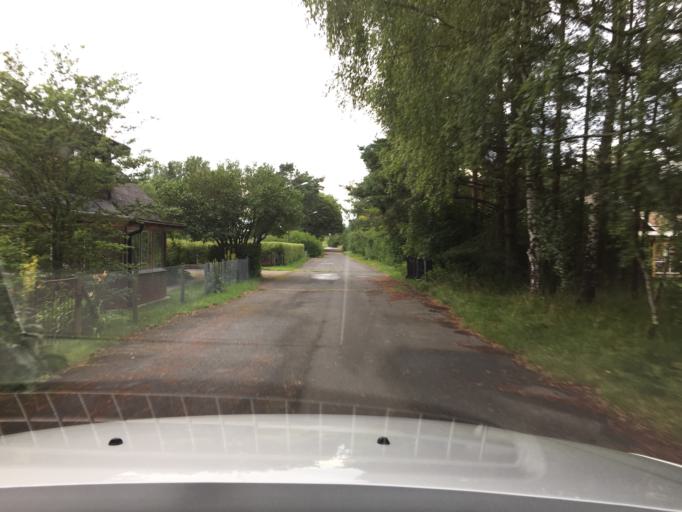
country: SE
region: Skane
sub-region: Kristianstads Kommun
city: Norra Asum
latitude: 55.9340
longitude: 14.0756
